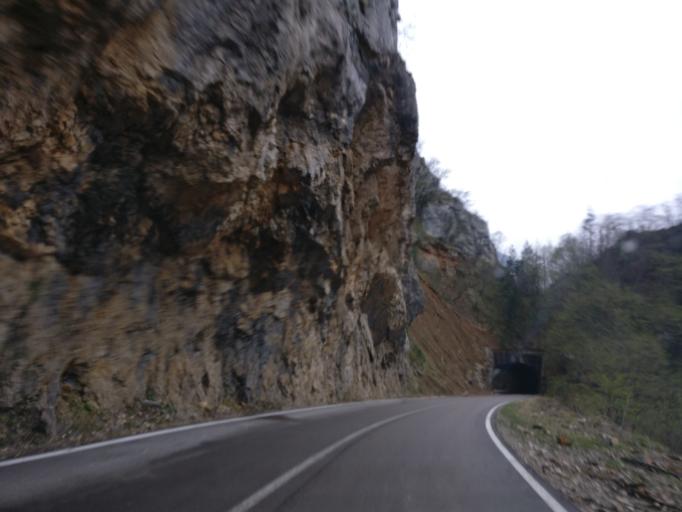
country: ME
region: Opstina Pluzine
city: Pluzine
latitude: 43.2553
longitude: 18.8370
